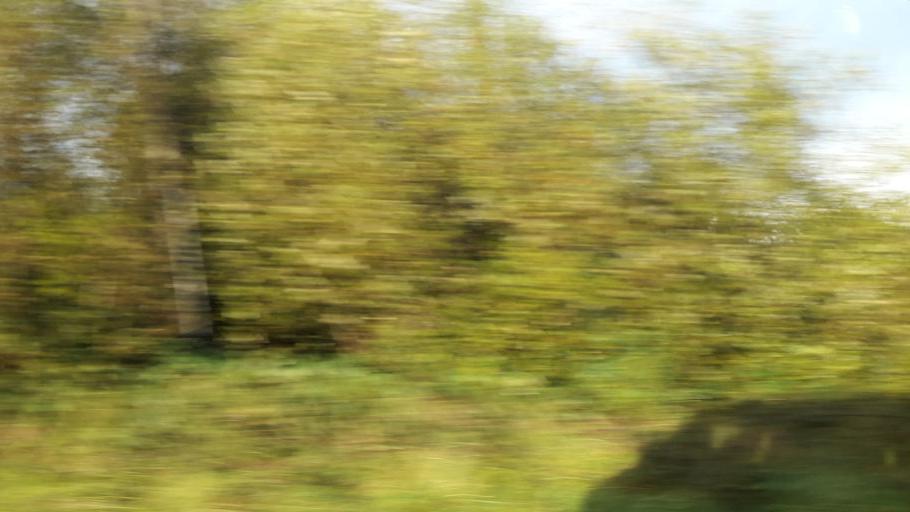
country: IE
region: Leinster
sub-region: An Longfort
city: Lanesborough
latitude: 53.7502
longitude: -7.9528
